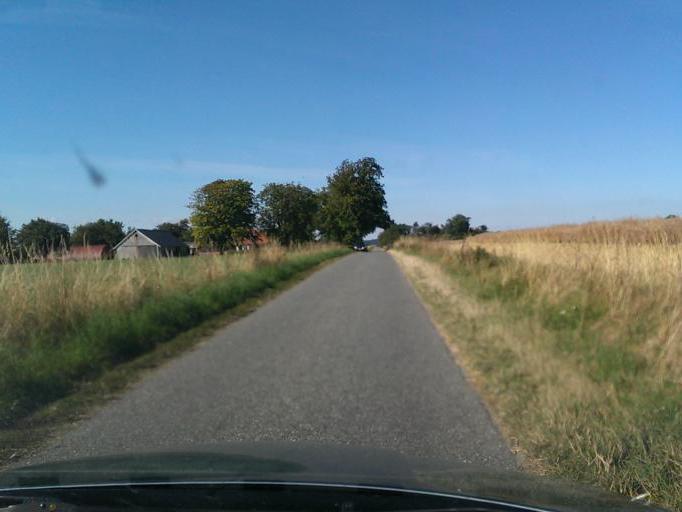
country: DK
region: Central Jutland
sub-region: Hedensted Kommune
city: Juelsminde
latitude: 55.8460
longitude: 10.0477
